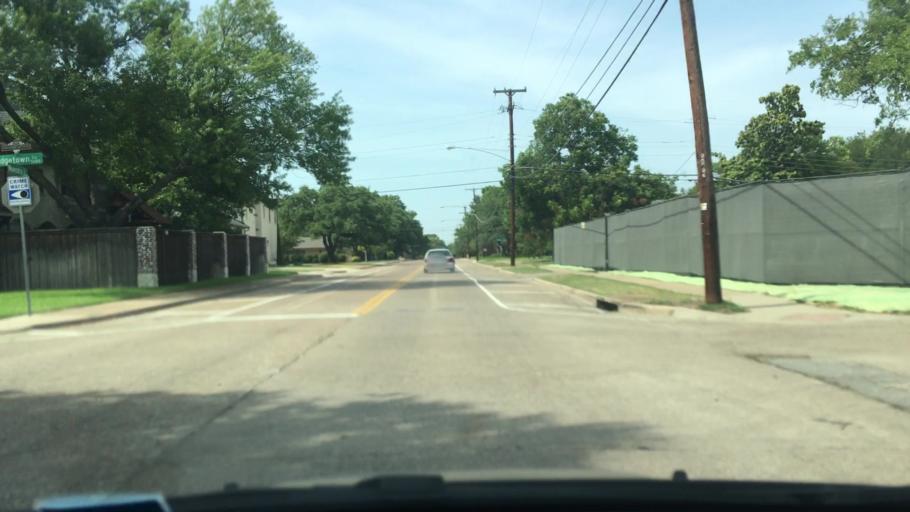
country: US
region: Texas
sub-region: Dallas County
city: Addison
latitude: 32.9116
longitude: -96.8117
